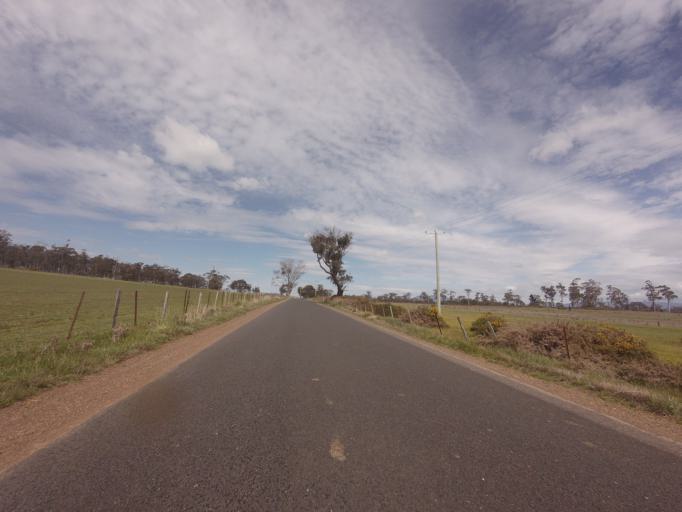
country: AU
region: Tasmania
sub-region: Northern Midlands
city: Longford
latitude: -41.7255
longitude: 147.1917
